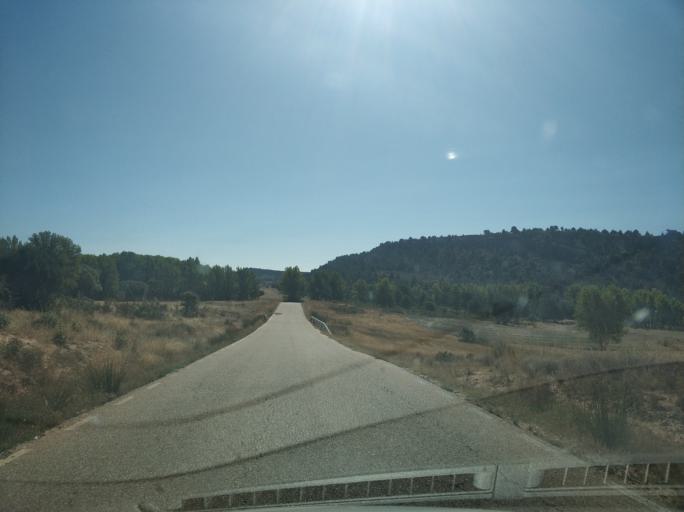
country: ES
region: Castille and Leon
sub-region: Provincia de Soria
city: Espeja de San Marcelino
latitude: 41.7887
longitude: -3.2015
